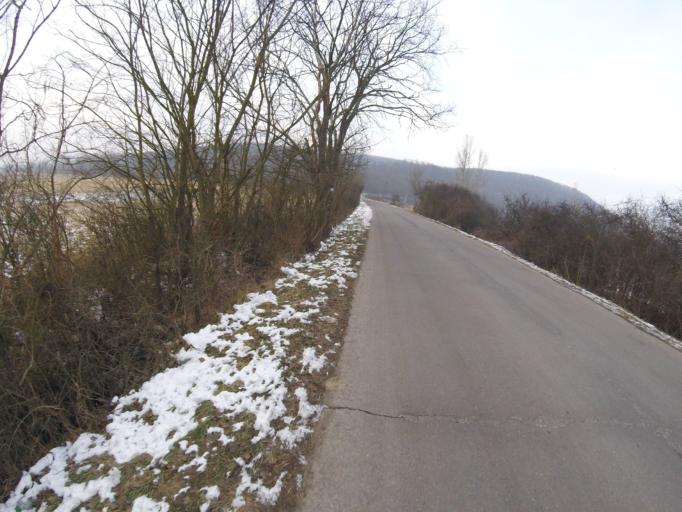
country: HU
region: Heves
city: Sirok
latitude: 47.9187
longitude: 20.1773
